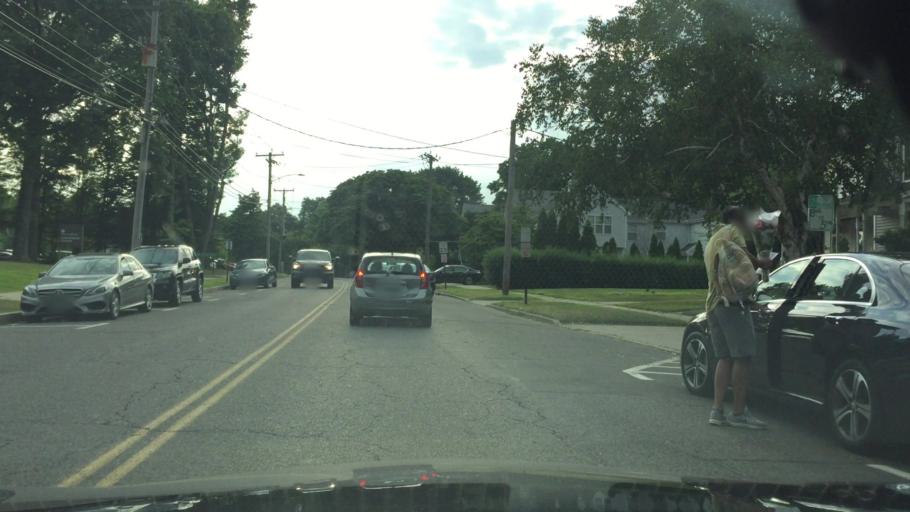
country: US
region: Connecticut
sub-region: New Haven County
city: City of Milford (balance)
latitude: 41.2268
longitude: -73.0598
